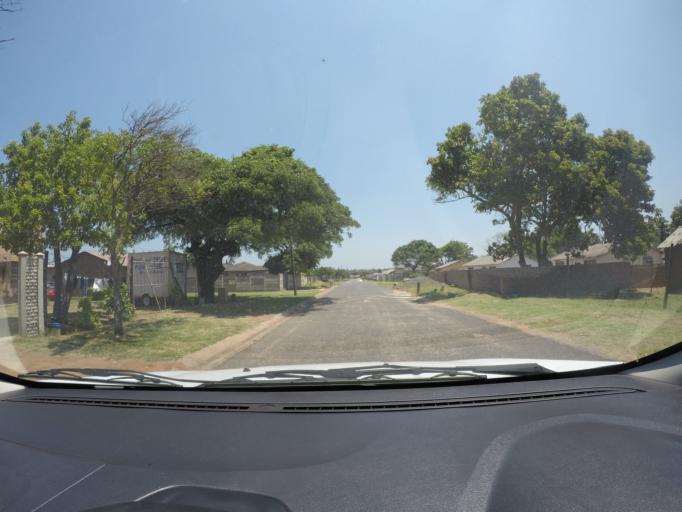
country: ZA
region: KwaZulu-Natal
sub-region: uThungulu District Municipality
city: eSikhawini
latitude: -28.8843
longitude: 31.8896
